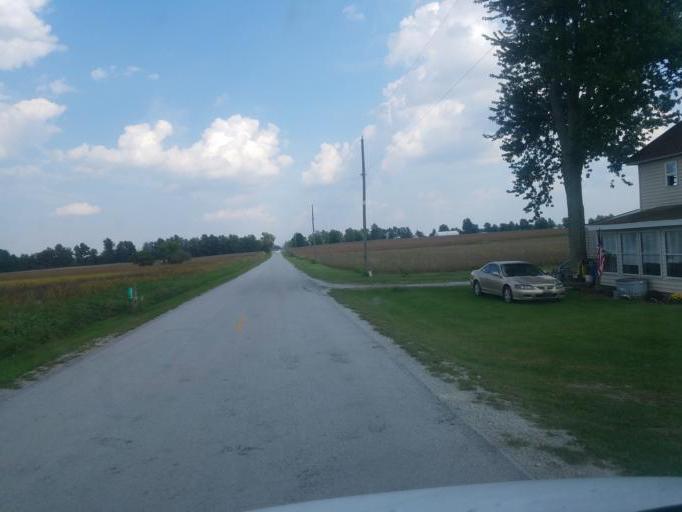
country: US
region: Ohio
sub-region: Hancock County
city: Arlington
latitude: 40.8125
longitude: -83.6802
